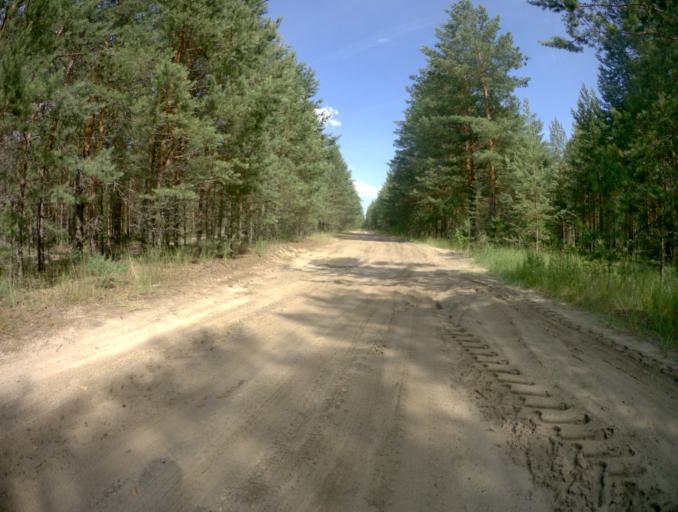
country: RU
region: Ivanovo
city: Talitsy
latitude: 56.5311
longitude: 42.3021
